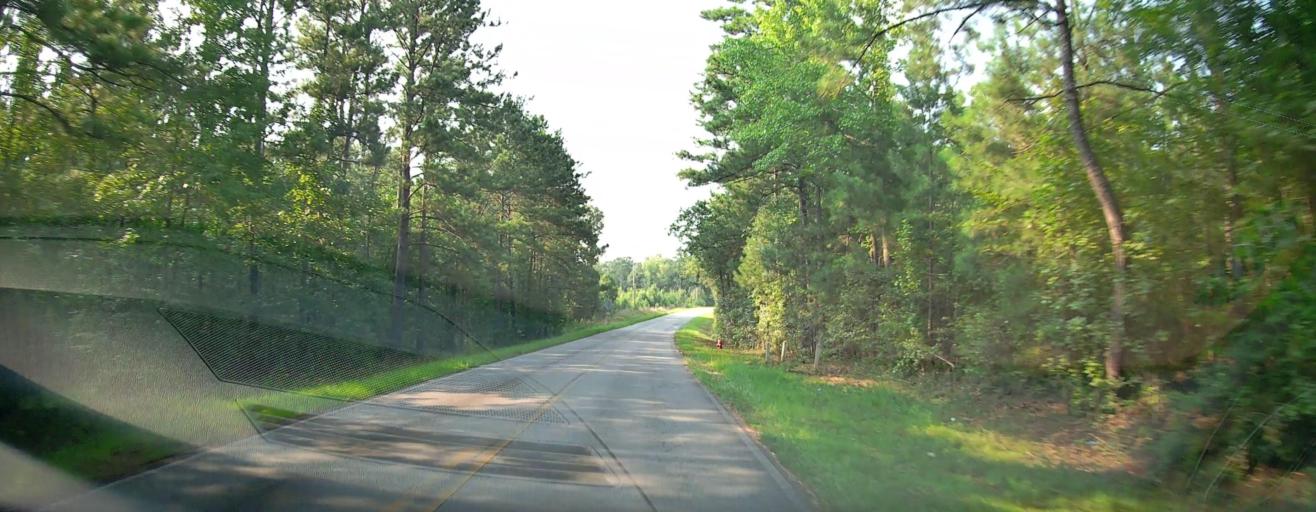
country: US
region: Georgia
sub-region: Monroe County
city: Forsyth
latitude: 32.9913
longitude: -83.7745
